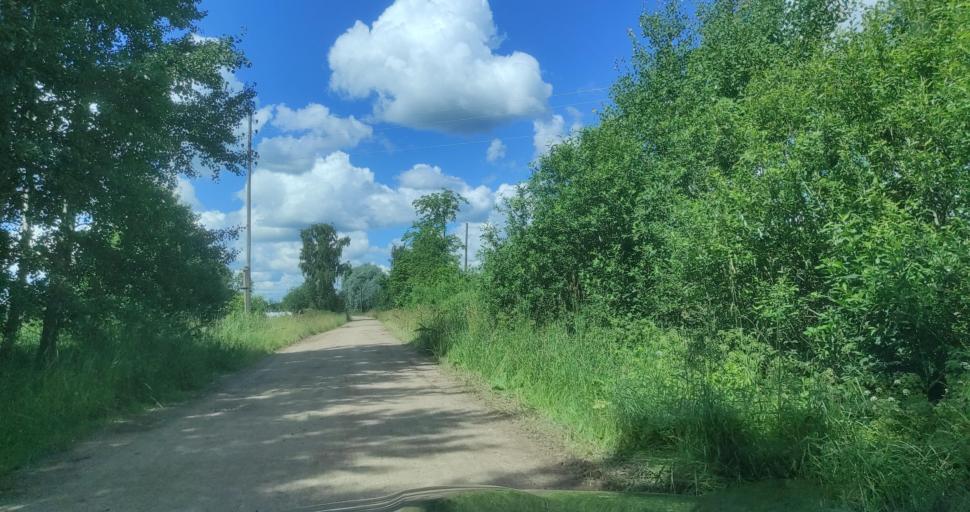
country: LV
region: Kuldigas Rajons
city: Kuldiga
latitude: 57.0017
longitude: 22.1397
